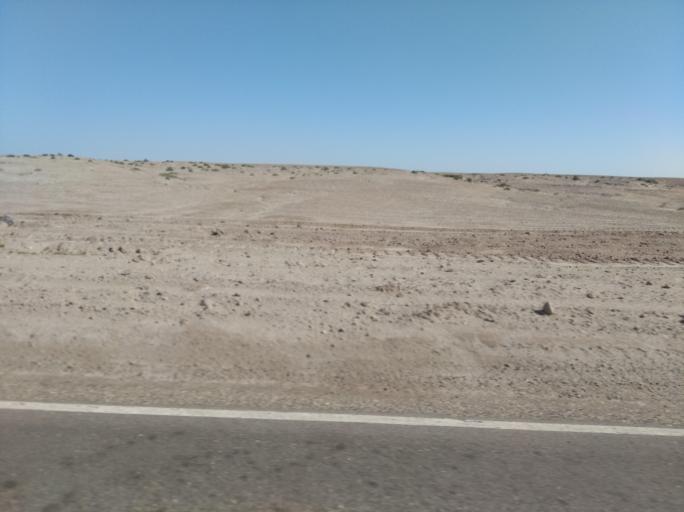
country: CL
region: Atacama
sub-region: Provincia de Copiapo
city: Copiapo
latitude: -27.3212
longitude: -70.8183
